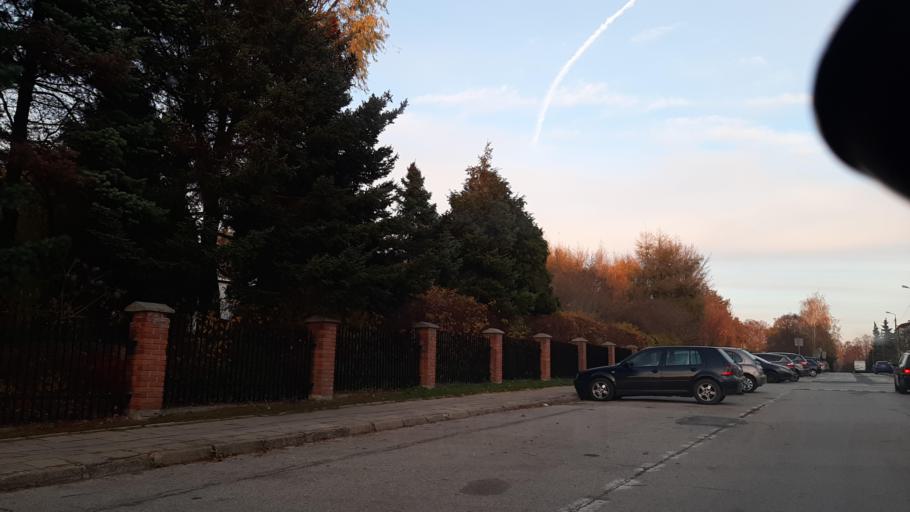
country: PL
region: Lublin Voivodeship
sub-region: Powiat lubelski
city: Lublin
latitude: 51.2701
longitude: 22.5062
